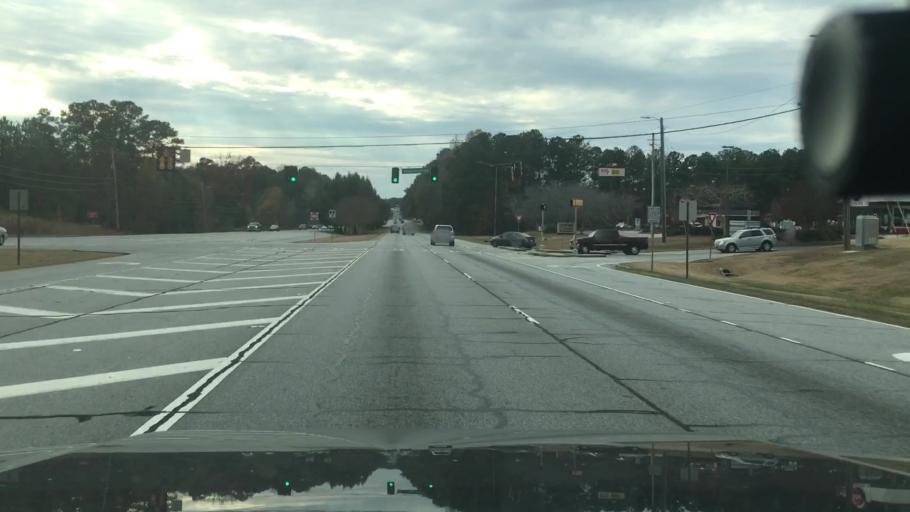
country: US
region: Georgia
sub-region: Coweta County
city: Newnan
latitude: 33.3911
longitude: -84.7707
